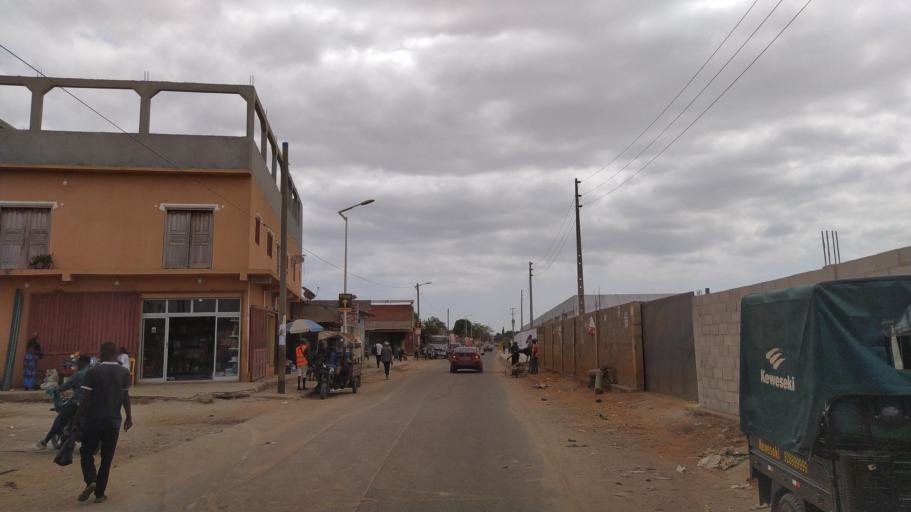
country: AO
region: Luanda
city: Luanda
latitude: -8.9323
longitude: 13.2603
